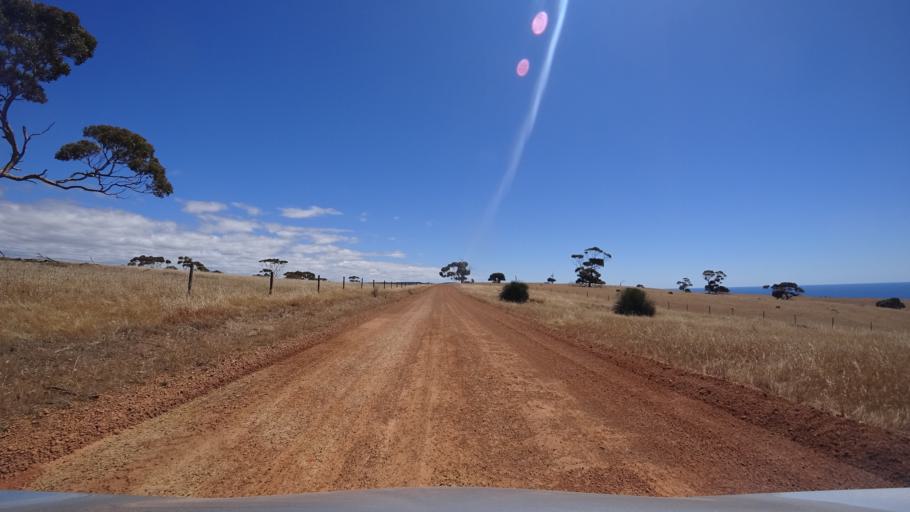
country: AU
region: South Australia
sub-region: Kangaroo Island
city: Kingscote
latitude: -35.6785
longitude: 136.9880
